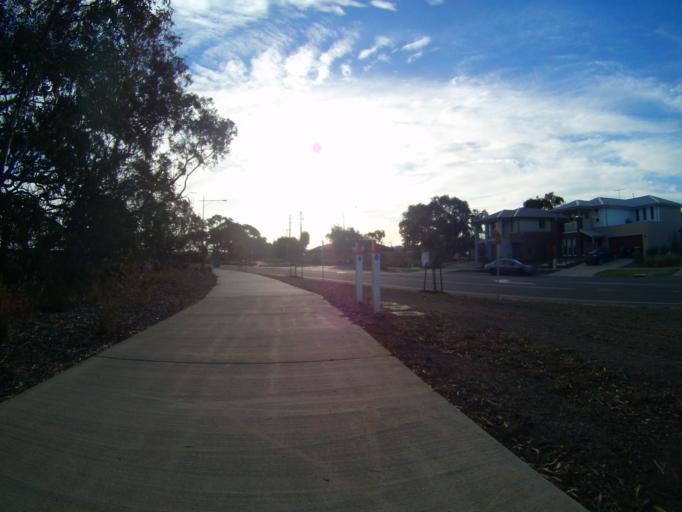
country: AU
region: Victoria
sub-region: Greater Geelong
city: Breakwater
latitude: -38.2382
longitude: 144.3724
